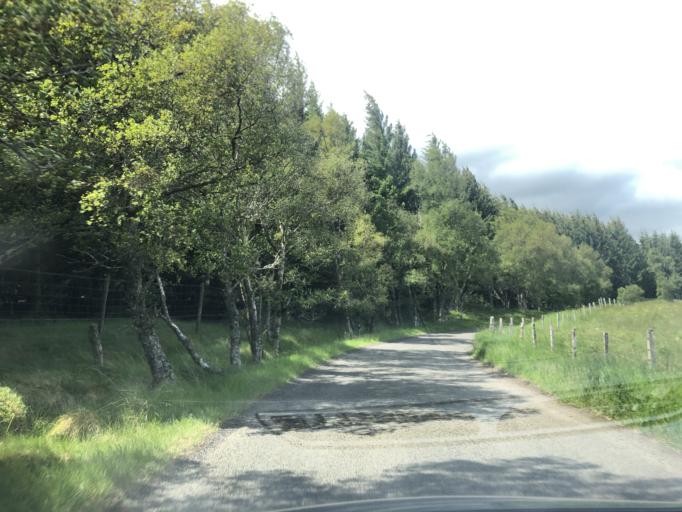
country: GB
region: Scotland
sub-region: Angus
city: Kirriemuir
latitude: 56.8270
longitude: -3.0681
